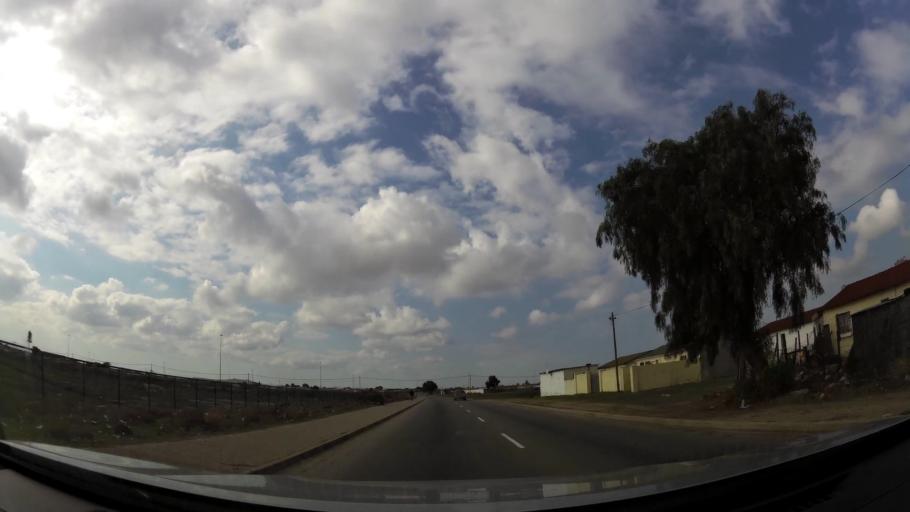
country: ZA
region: Eastern Cape
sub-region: Nelson Mandela Bay Metropolitan Municipality
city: Port Elizabeth
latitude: -33.8067
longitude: 25.5889
